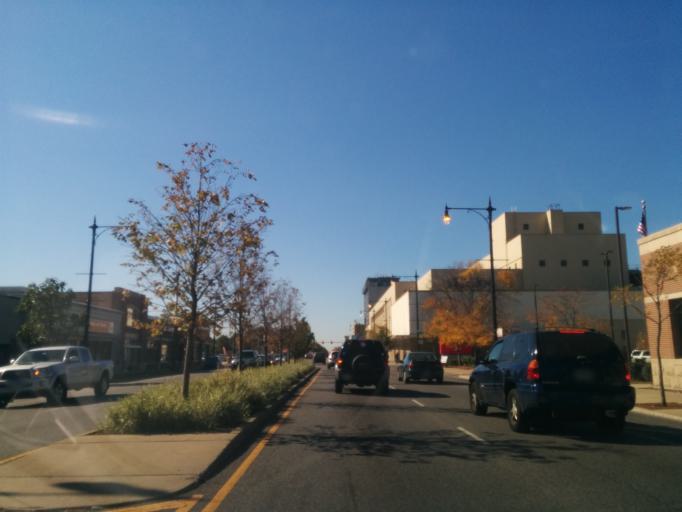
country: US
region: Illinois
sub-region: Cook County
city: Elmwood Park
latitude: 41.9090
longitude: -87.8030
